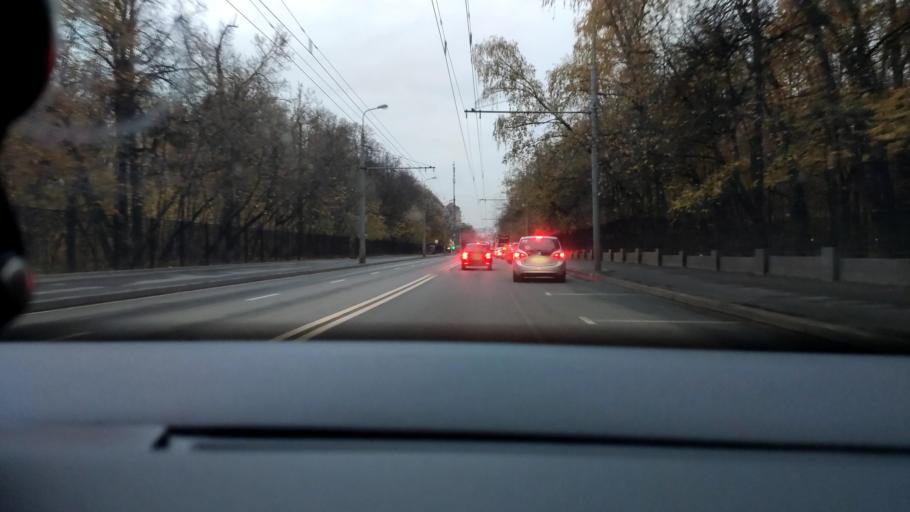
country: RU
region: Moskovskaya
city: Fili
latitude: 55.7493
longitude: 37.4929
